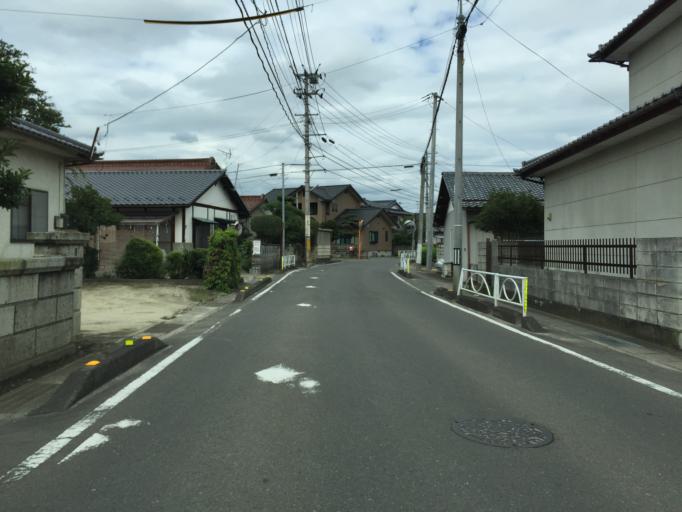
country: JP
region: Fukushima
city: Hobaramachi
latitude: 37.8121
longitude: 140.4956
